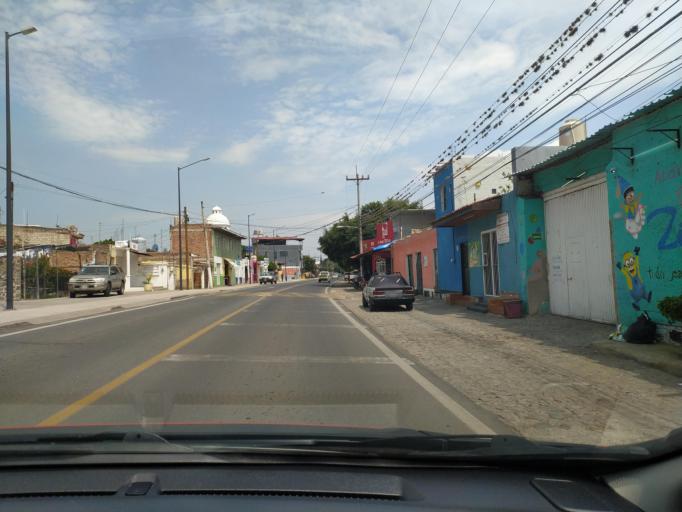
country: MX
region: Jalisco
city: San Juan Cosala
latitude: 20.2876
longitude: -103.3383
